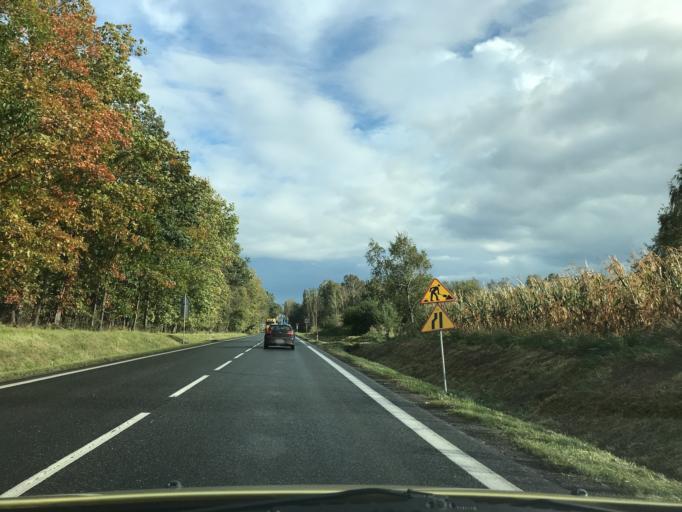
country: PL
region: Greater Poland Voivodeship
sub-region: Kalisz
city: Kalisz
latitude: 51.7744
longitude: 18.0270
